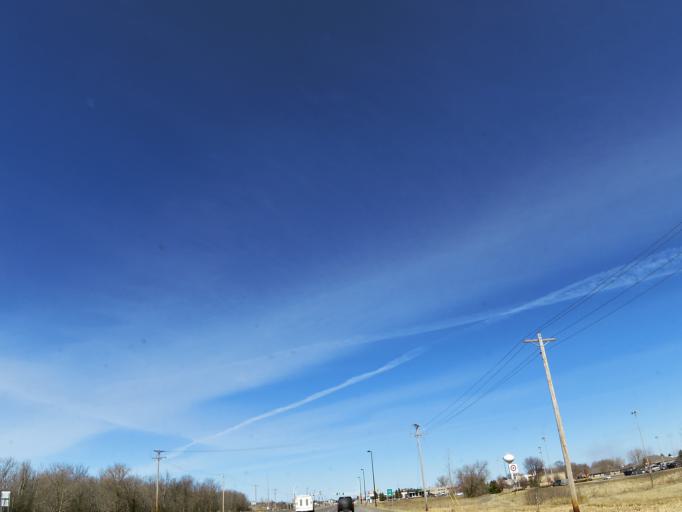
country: US
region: Minnesota
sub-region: Wright County
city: Buffalo
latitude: 45.1626
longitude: -93.8568
